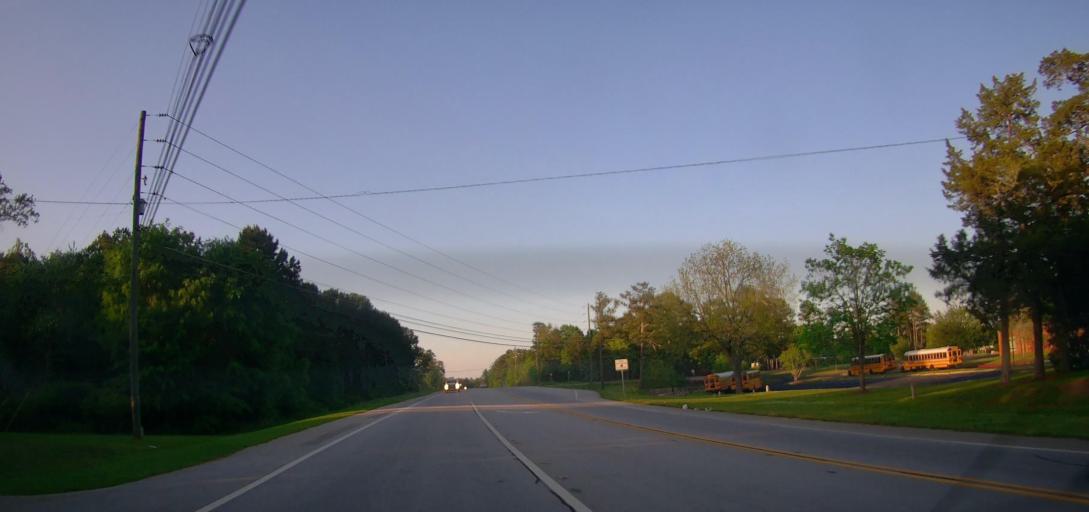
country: US
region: Georgia
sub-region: Newton County
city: Oakwood
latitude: 33.5390
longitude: -83.9513
